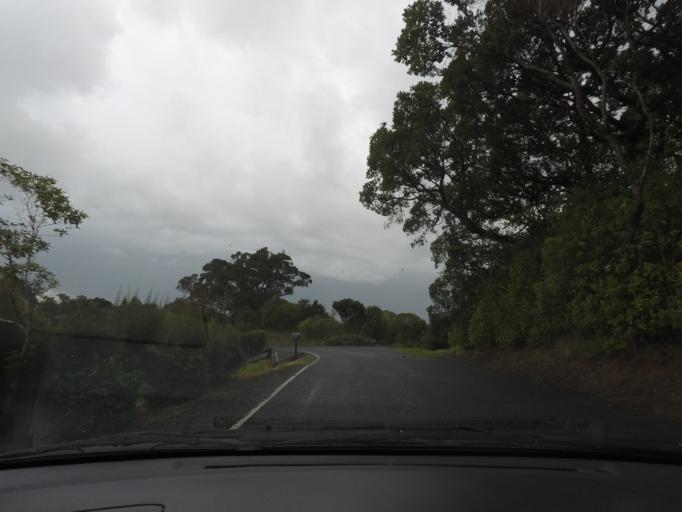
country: NZ
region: Auckland
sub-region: Auckland
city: Warkworth
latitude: -36.4750
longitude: 174.7338
